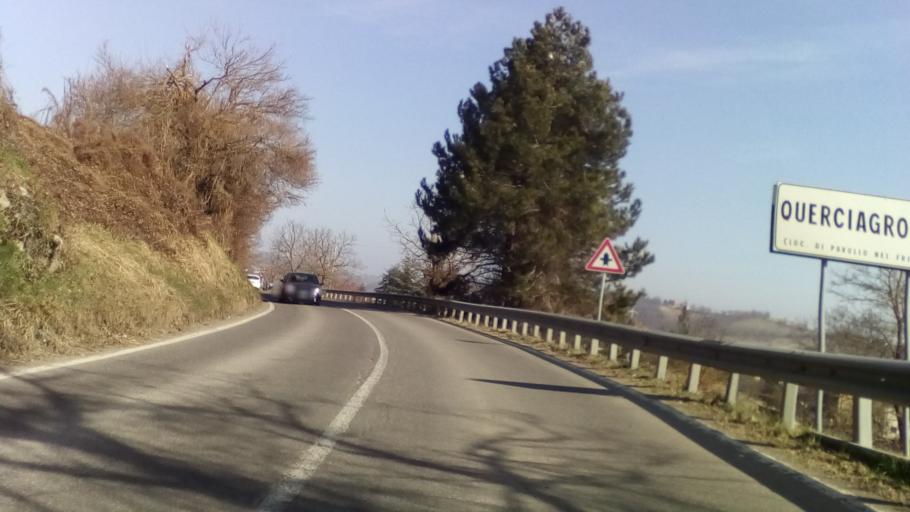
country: IT
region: Emilia-Romagna
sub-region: Provincia di Modena
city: Pavullo nel Frignano
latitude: 44.3108
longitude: 10.8233
